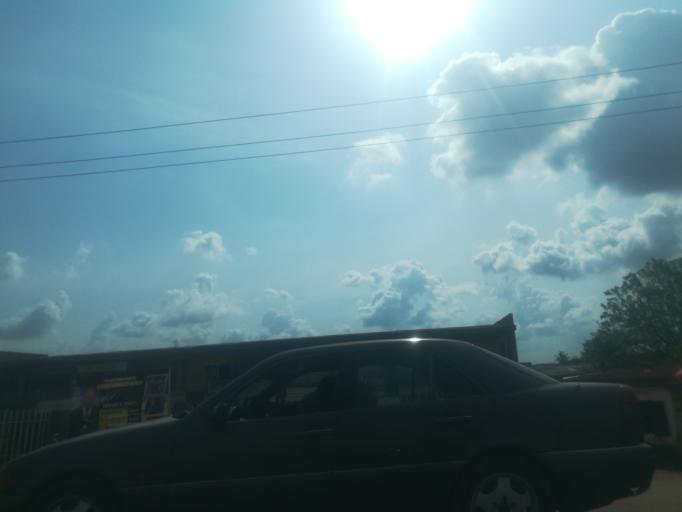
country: NG
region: Oyo
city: Ibadan
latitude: 7.3877
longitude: 3.8228
